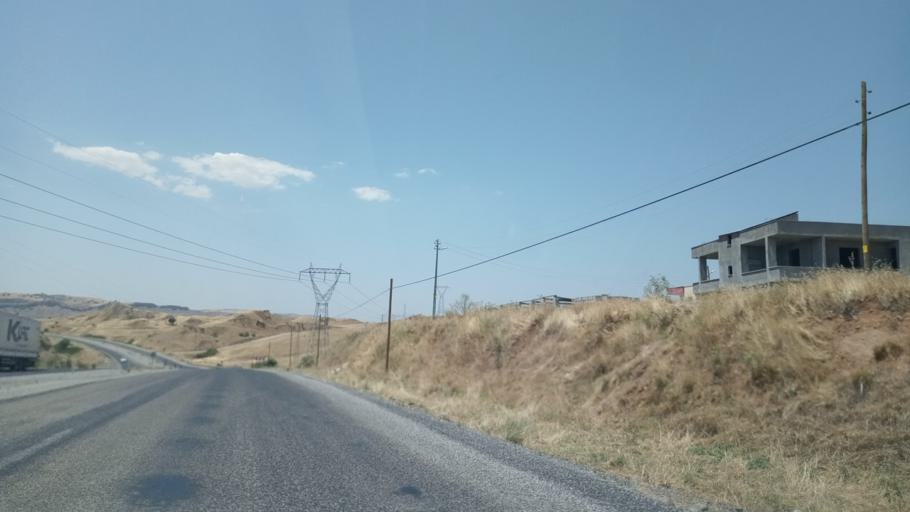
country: TR
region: Batman
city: Kozluk
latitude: 38.1657
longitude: 41.4258
